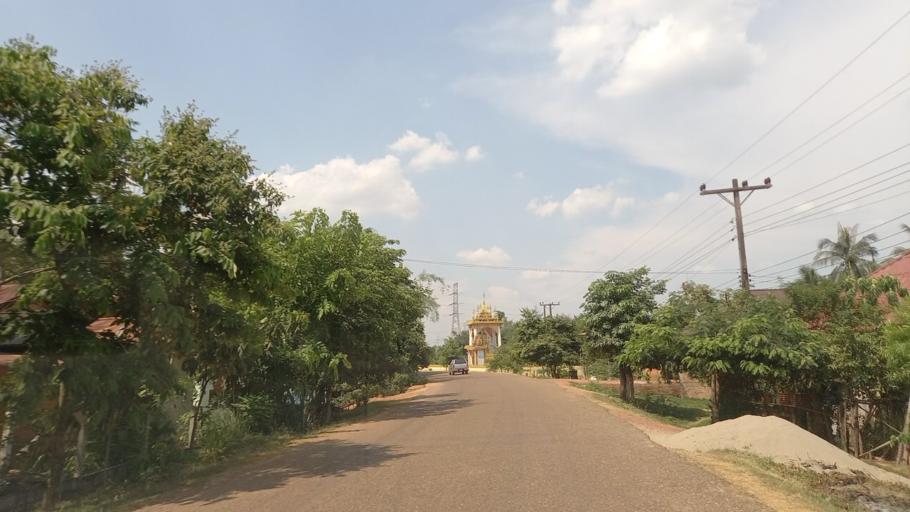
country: LA
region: Bolikhamxai
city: Muang Pakxan
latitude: 18.4074
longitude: 103.7009
